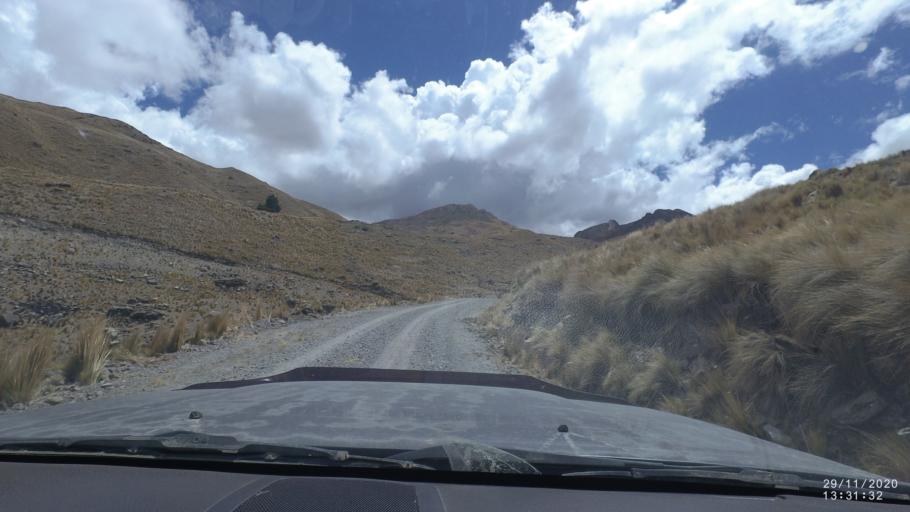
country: BO
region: Cochabamba
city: Cochabamba
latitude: -17.1059
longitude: -66.3440
